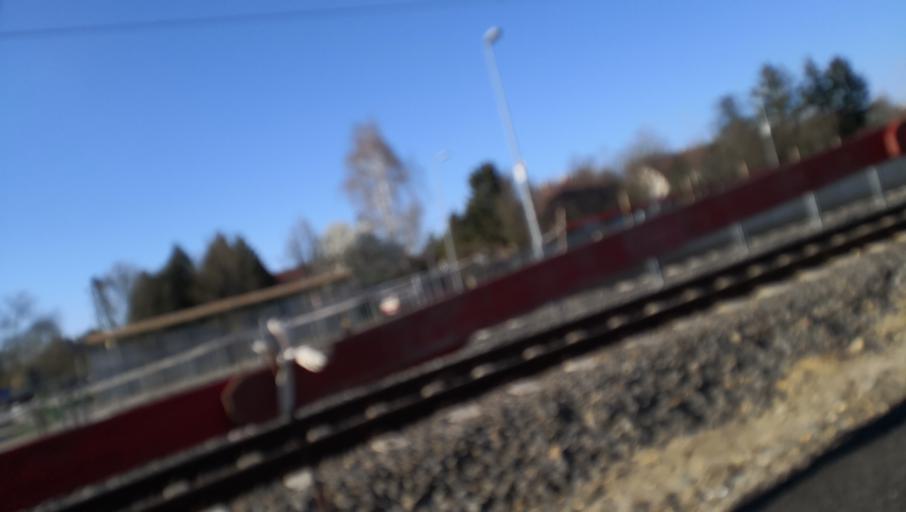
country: HU
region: Budapest
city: Budapest XVII. keruelet
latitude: 47.4912
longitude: 19.2826
